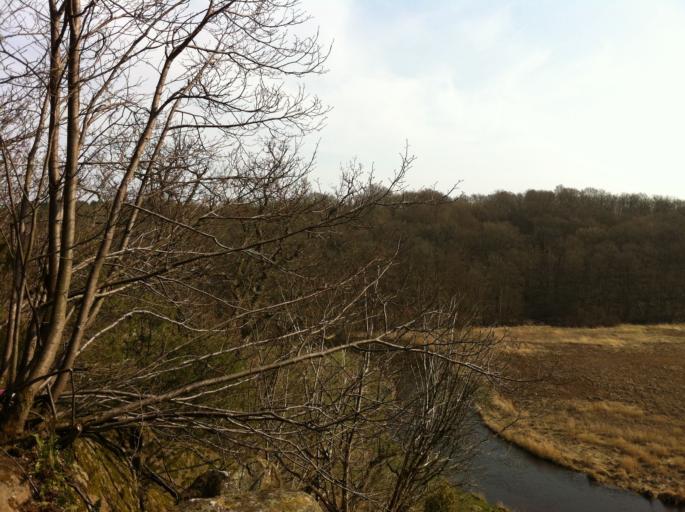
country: SE
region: Skane
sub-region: Eslovs Kommun
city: Stehag
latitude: 56.0097
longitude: 13.3878
